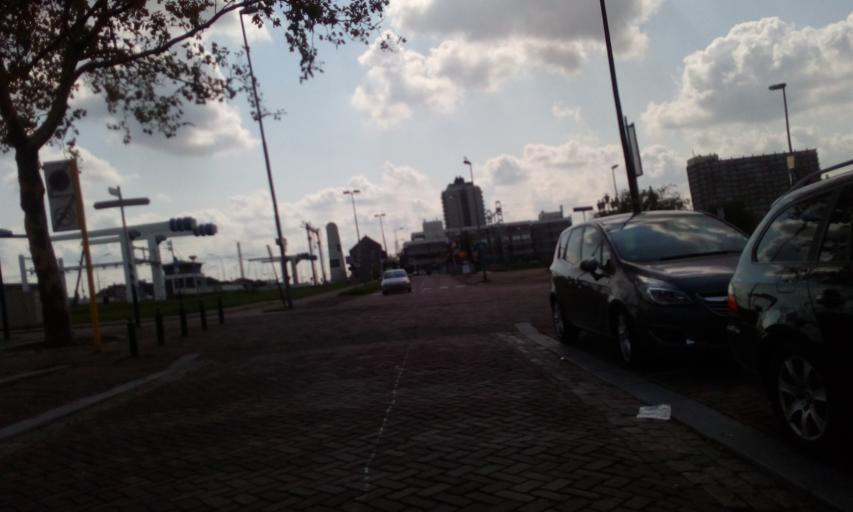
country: NL
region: South Holland
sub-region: Gemeente Vlaardingen
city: Vlaardingen
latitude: 51.9046
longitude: 4.3460
